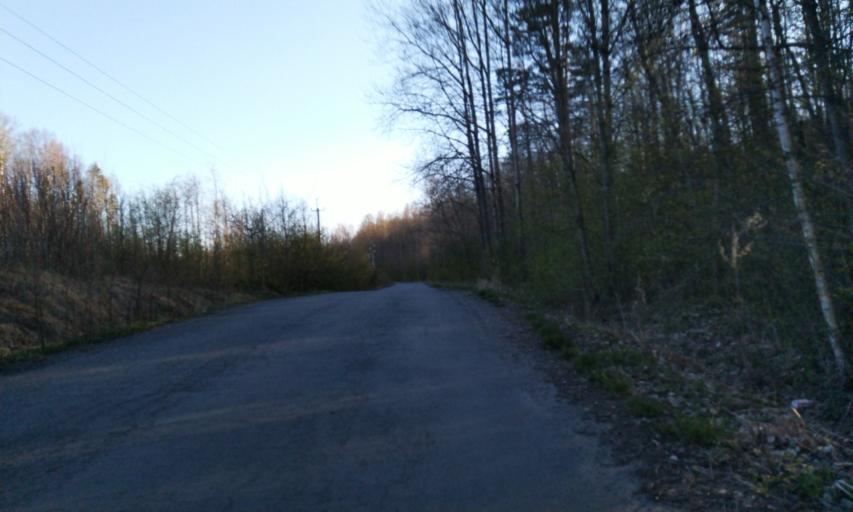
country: RU
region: Leningrad
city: Toksovo
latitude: 60.1434
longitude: 30.5728
